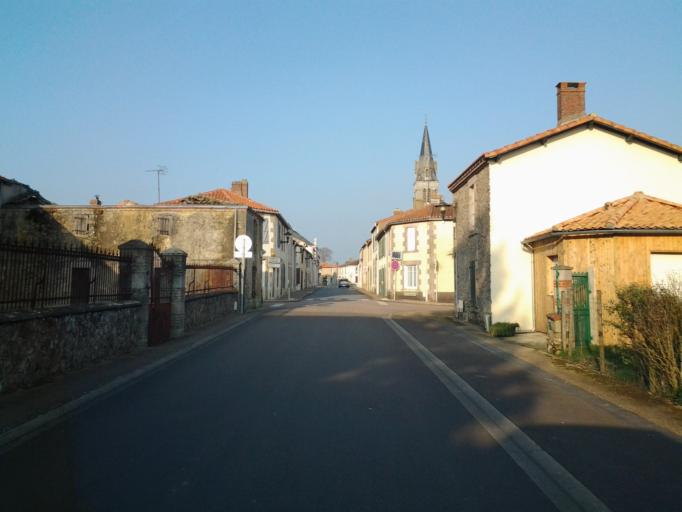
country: FR
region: Pays de la Loire
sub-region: Departement de la Vendee
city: La Chaize-le-Vicomte
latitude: 46.6583
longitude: -1.2335
